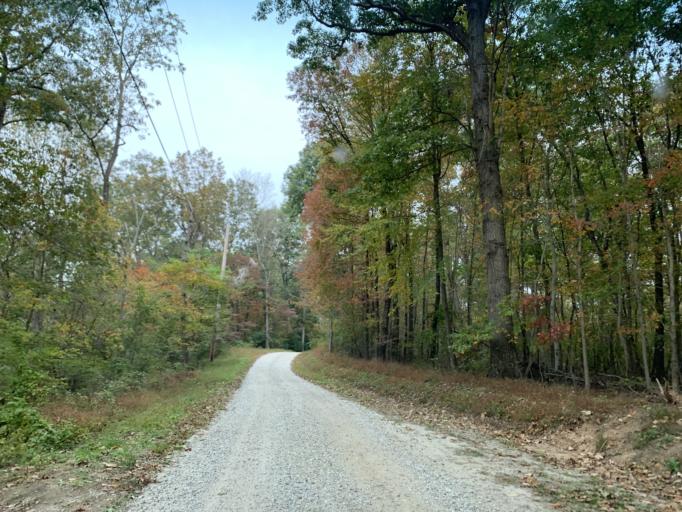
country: US
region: Pennsylvania
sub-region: York County
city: Susquehanna Trails
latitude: 39.7988
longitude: -76.4292
